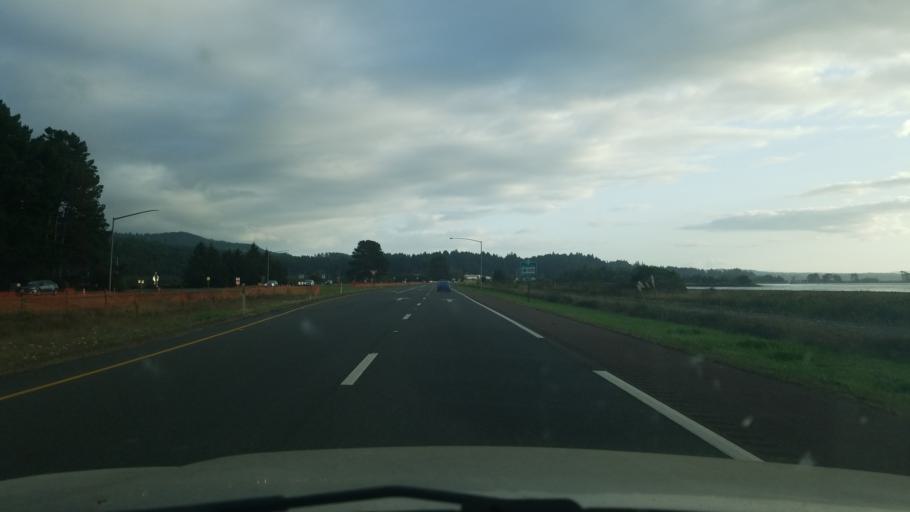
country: US
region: California
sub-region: Humboldt County
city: Bayside
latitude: 40.8364
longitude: -124.0822
